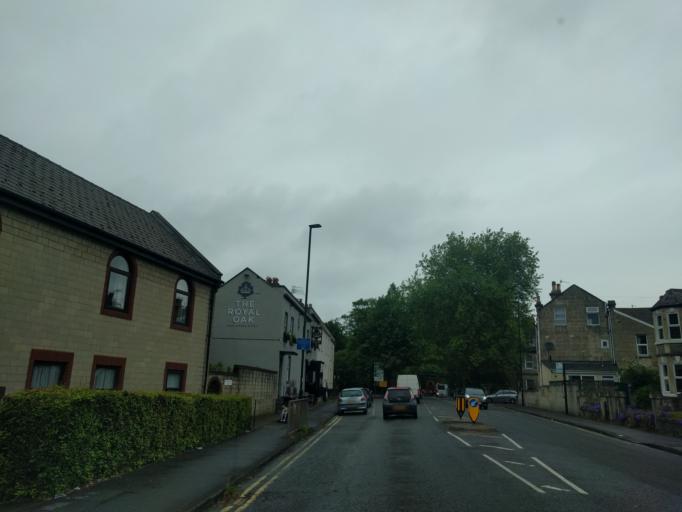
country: GB
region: England
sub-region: Bath and North East Somerset
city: Bath
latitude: 51.3792
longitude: -2.3511
